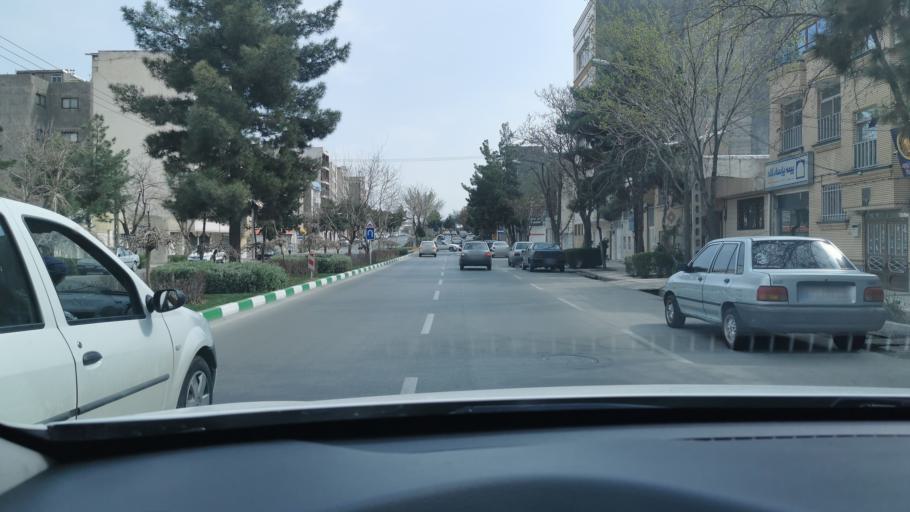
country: IR
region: Razavi Khorasan
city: Mashhad
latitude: 36.2773
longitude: 59.5658
